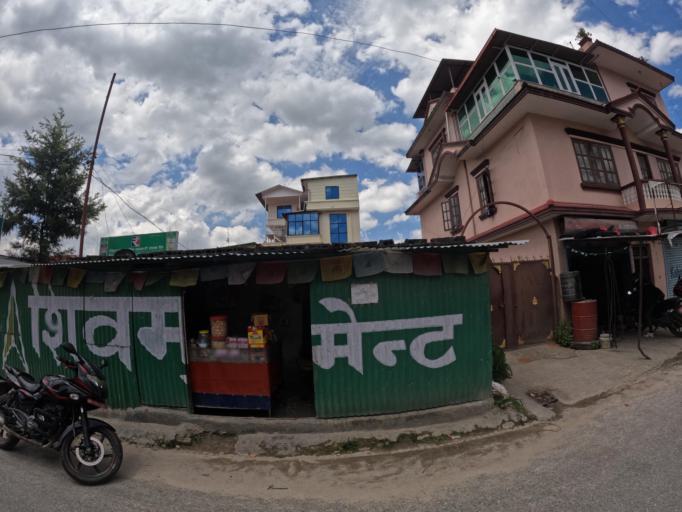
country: NP
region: Central Region
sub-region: Bagmati Zone
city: Kathmandu
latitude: 27.7784
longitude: 85.3257
